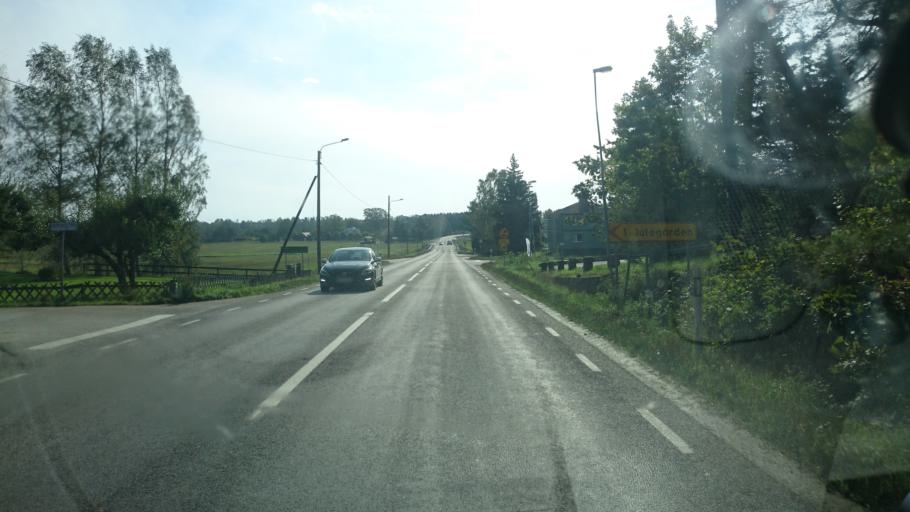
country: SE
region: Vaestra Goetaland
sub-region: Vanersborgs Kommun
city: Vargon
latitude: 58.2516
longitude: 12.4166
